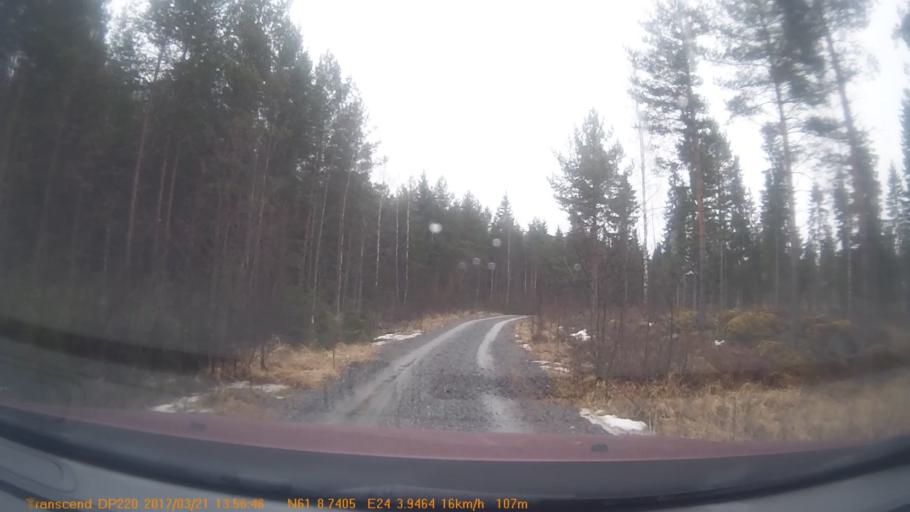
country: FI
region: Haeme
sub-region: Haemeenlinna
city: Kalvola
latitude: 61.1457
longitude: 24.0657
